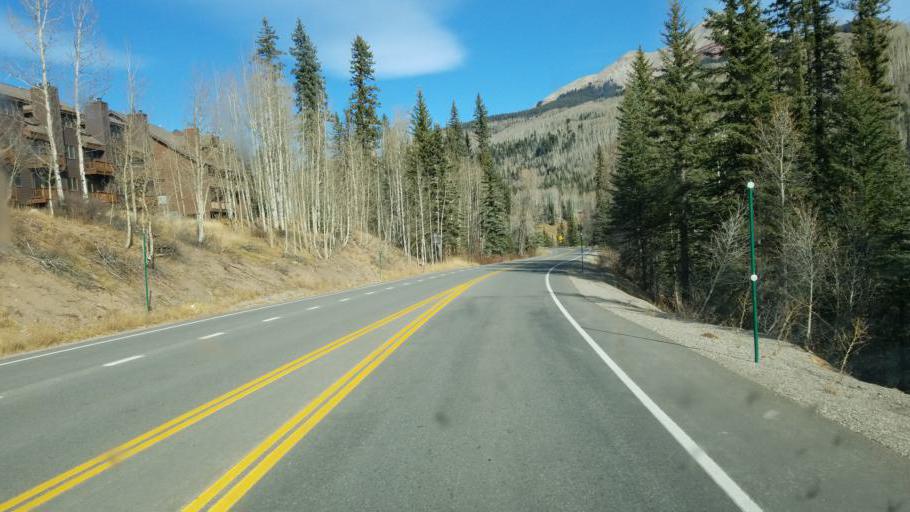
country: US
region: Colorado
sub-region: San Juan County
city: Silverton
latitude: 37.6549
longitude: -107.8105
